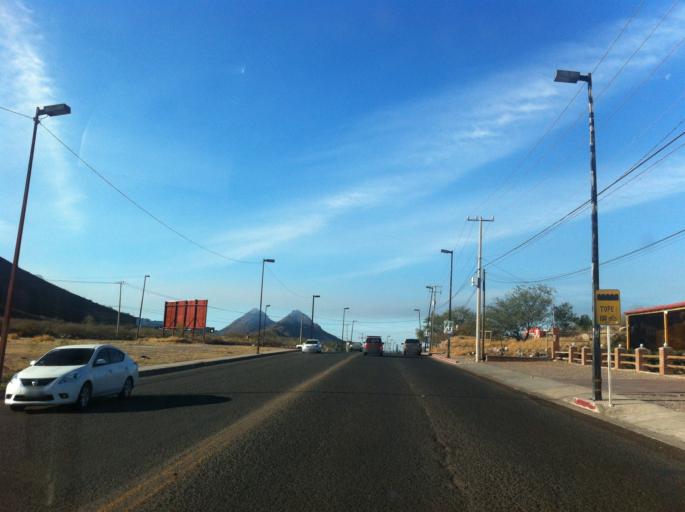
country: MX
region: Sonora
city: Heroica Guaymas
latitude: 27.9289
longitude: -110.9278
